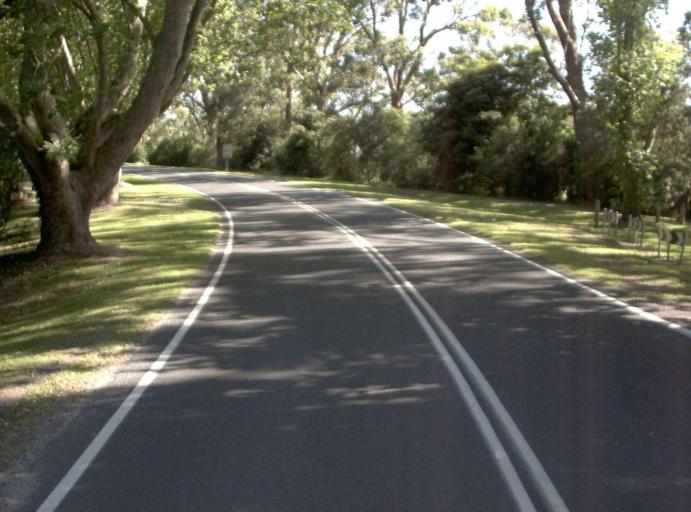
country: AU
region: Victoria
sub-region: East Gippsland
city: Lakes Entrance
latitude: -37.7109
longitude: 148.4529
